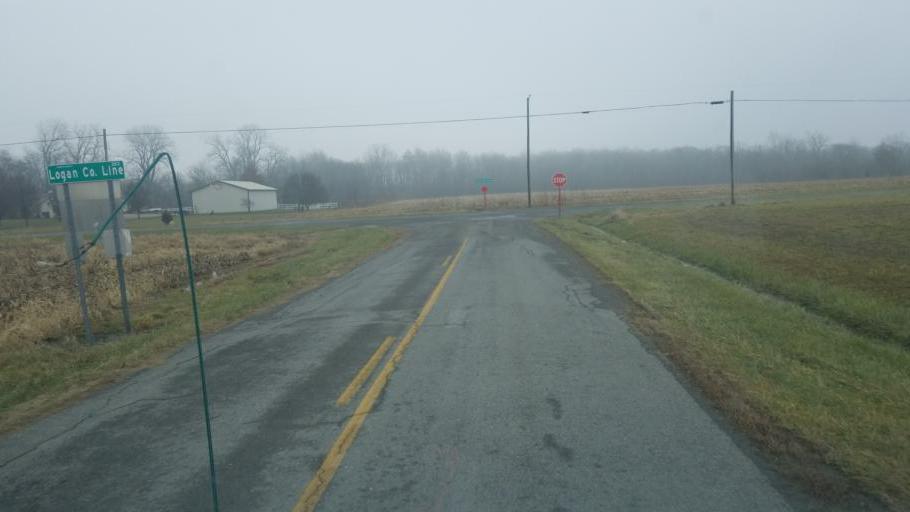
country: US
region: Ohio
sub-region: Hardin County
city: Kenton
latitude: 40.5033
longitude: -83.5208
